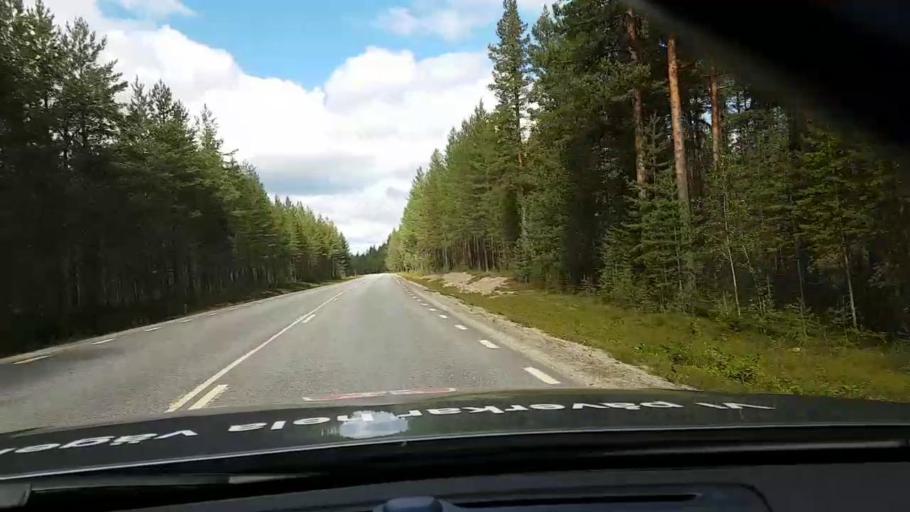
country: SE
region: Vaesternorrland
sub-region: OErnskoeldsviks Kommun
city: Bredbyn
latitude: 63.5332
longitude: 17.9669
